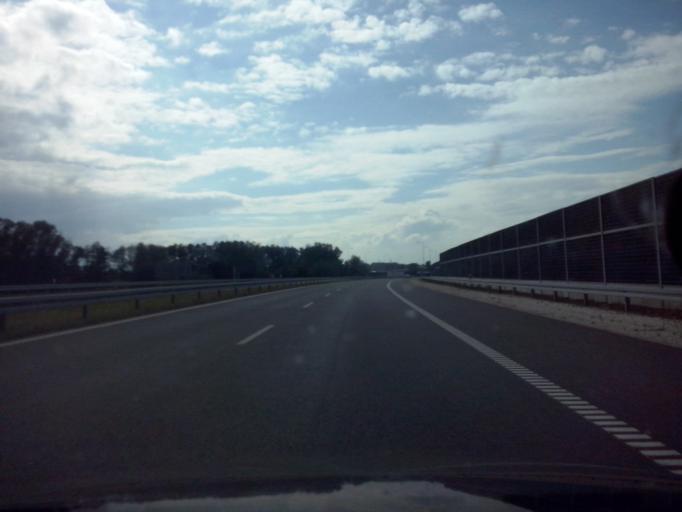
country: PL
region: Lesser Poland Voivodeship
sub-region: Powiat tarnowski
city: Lisia Gora
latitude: 50.0546
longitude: 21.0270
